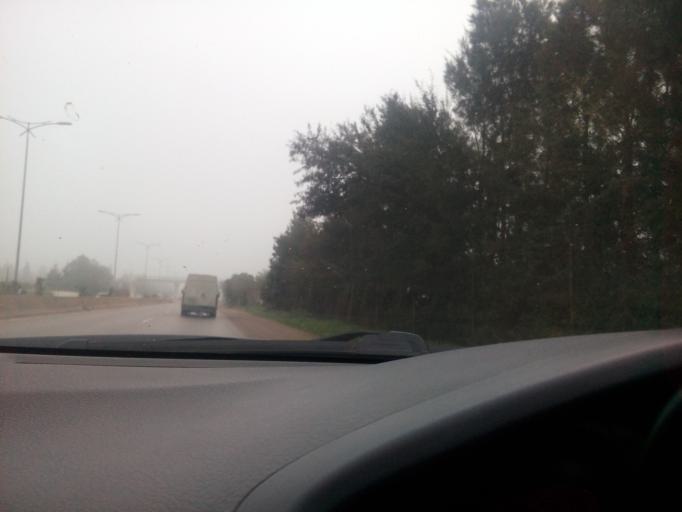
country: DZ
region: Oran
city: Bou Tlelis
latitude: 35.5727
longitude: -0.8708
